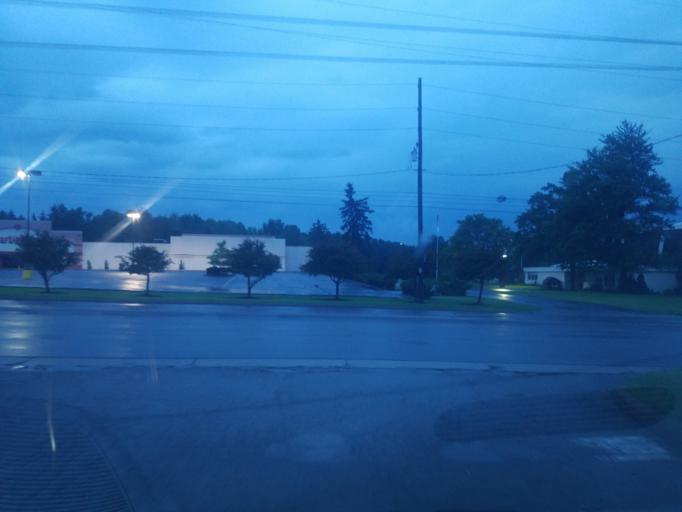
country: US
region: Ohio
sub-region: Mahoning County
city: Boardman
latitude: 41.0247
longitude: -80.6785
